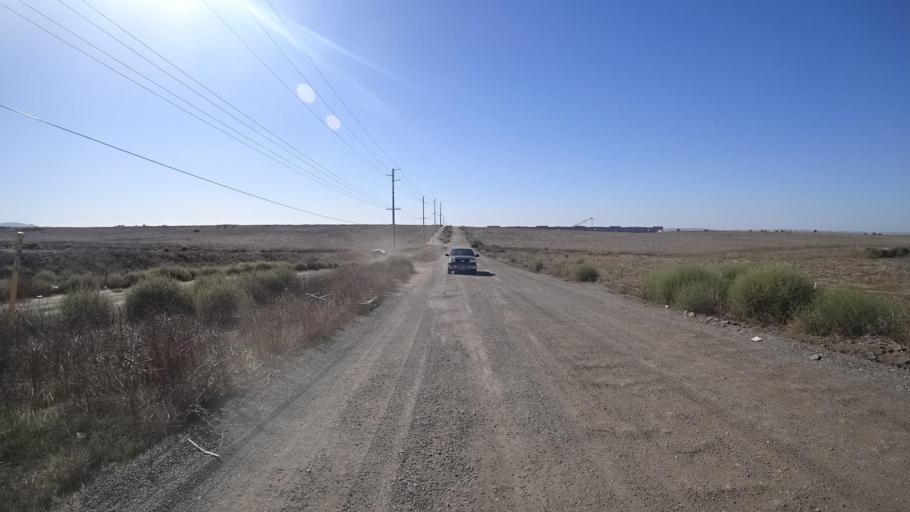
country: MX
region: Baja California
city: Tijuana
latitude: 32.5757
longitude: -116.9451
